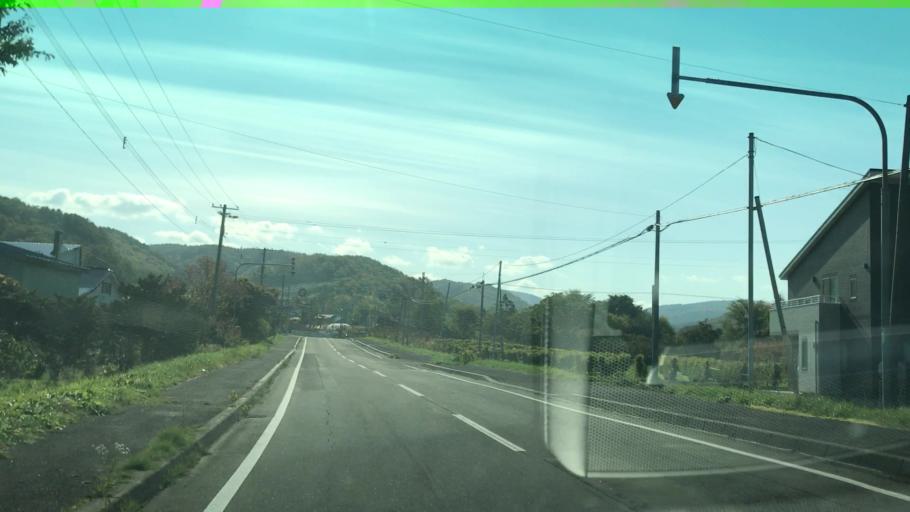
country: JP
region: Hokkaido
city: Yoichi
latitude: 43.1686
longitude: 140.8206
